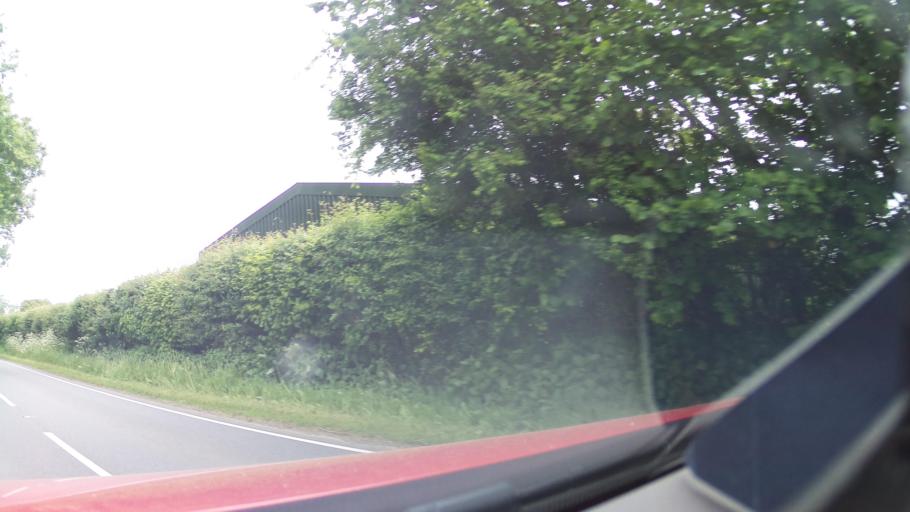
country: GB
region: England
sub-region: Dorset
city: Sherborne
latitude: 50.8581
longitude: -2.4718
